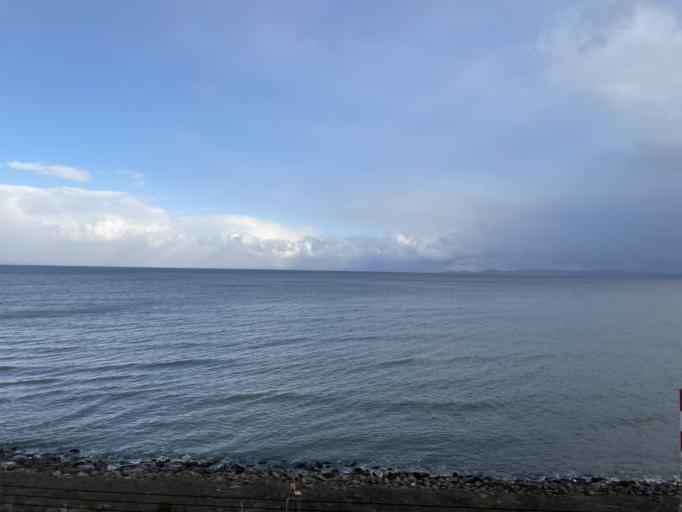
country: JP
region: Aomori
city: Aomori Shi
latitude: 41.0280
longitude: 140.6467
